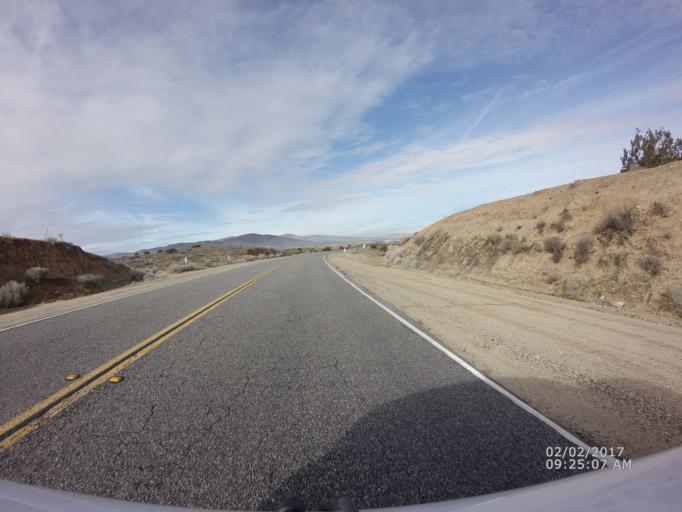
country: US
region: California
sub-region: Los Angeles County
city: Vincent
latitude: 34.5284
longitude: -118.0696
